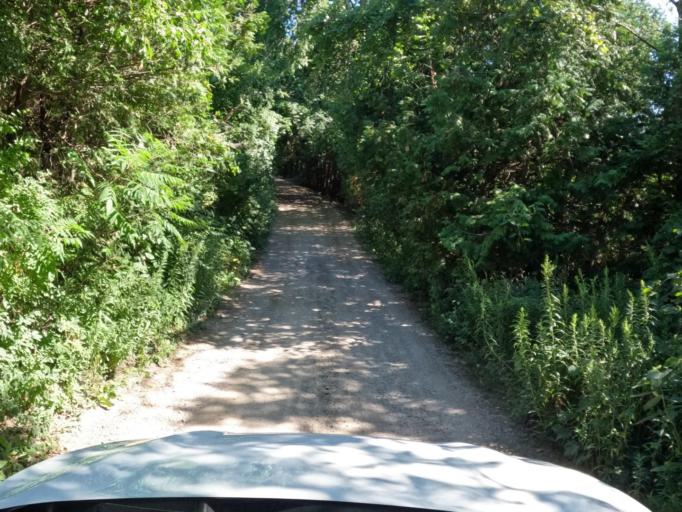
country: CA
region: Ontario
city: Cambridge
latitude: 43.4197
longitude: -80.2525
